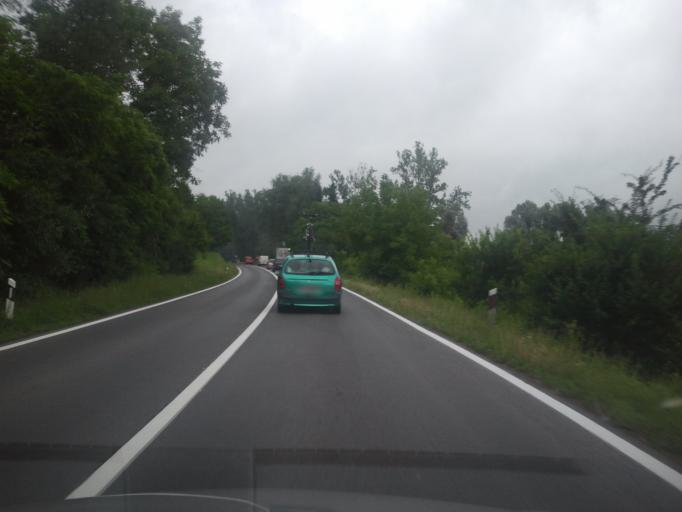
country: HR
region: Karlovacka
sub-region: Grad Karlovac
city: Karlovac
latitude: 45.4152
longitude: 15.6077
